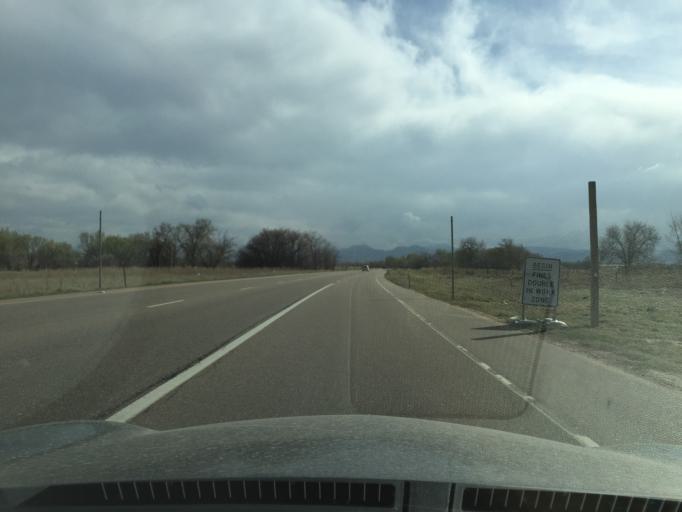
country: US
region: Colorado
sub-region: Boulder County
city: Niwot
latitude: 40.1304
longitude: -105.1412
